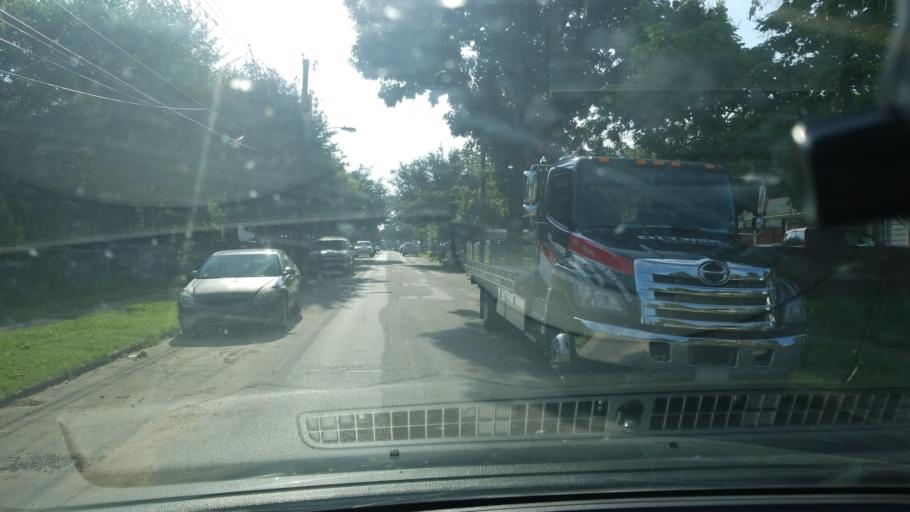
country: US
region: Texas
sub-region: Dallas County
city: Balch Springs
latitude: 32.7237
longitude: -96.6873
